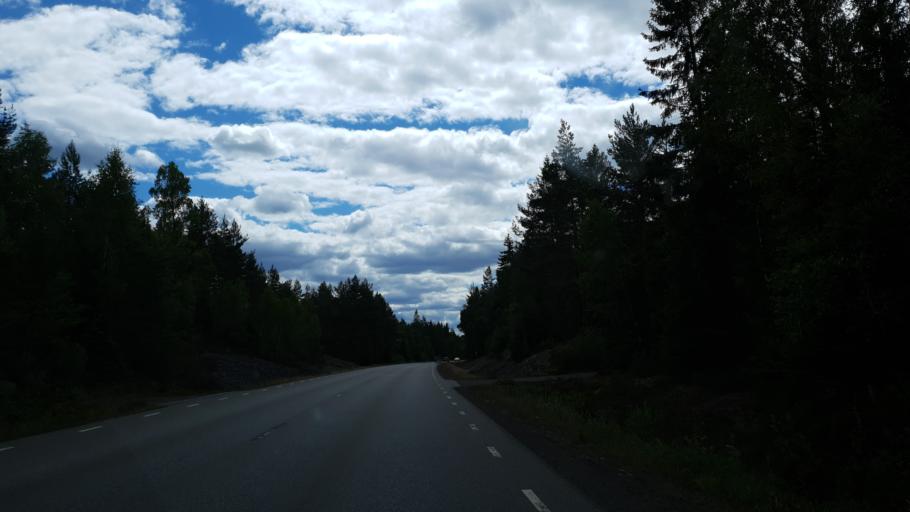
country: SE
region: Kronoberg
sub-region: Uppvidinge Kommun
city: Lenhovda
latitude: 56.9365
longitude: 15.5819
